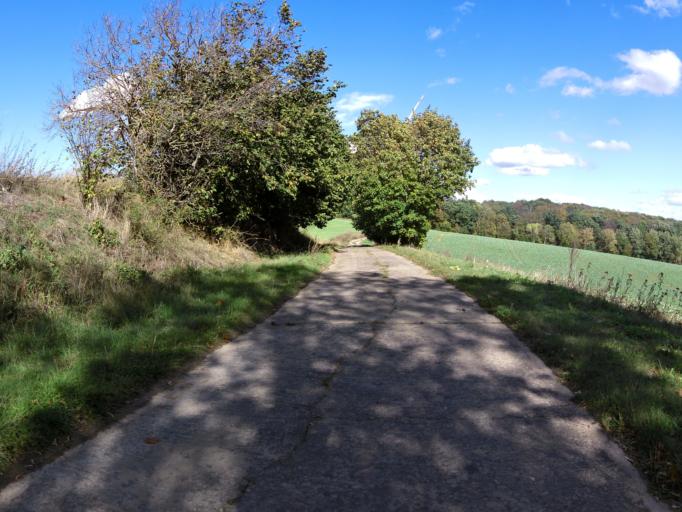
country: DE
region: Bavaria
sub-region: Regierungsbezirk Unterfranken
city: Hettstadt
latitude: 49.8269
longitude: 9.8288
